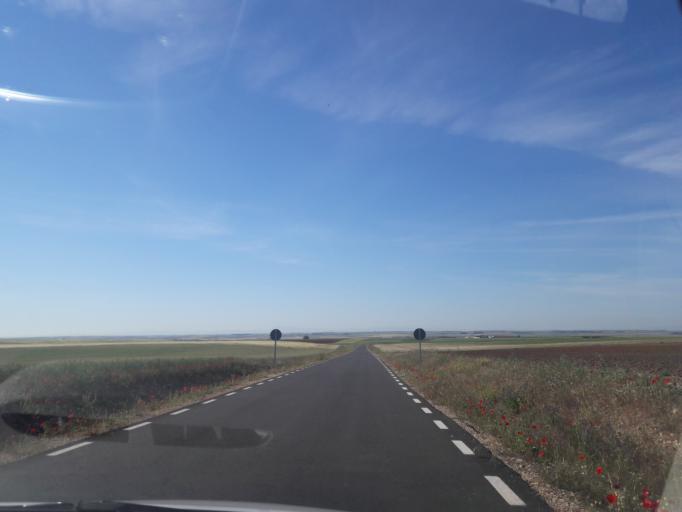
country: ES
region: Castille and Leon
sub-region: Provincia de Salamanca
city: Parada de Rubiales
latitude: 41.1435
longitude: -5.4316
